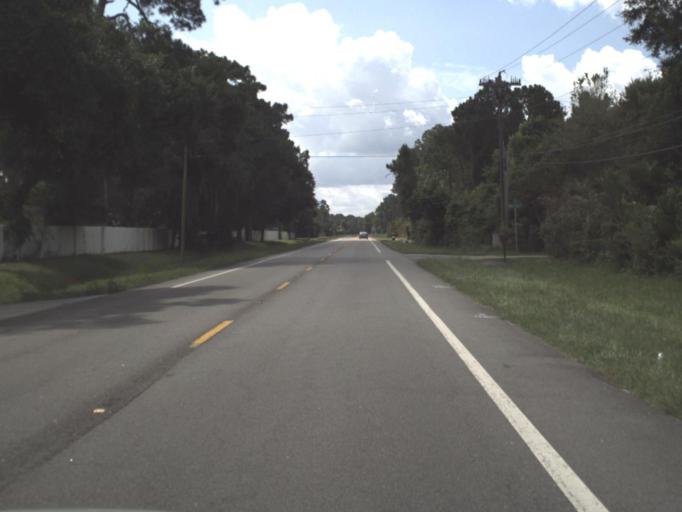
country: US
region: Florida
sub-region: Clay County
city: Green Cove Springs
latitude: 30.0014
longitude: -81.6037
